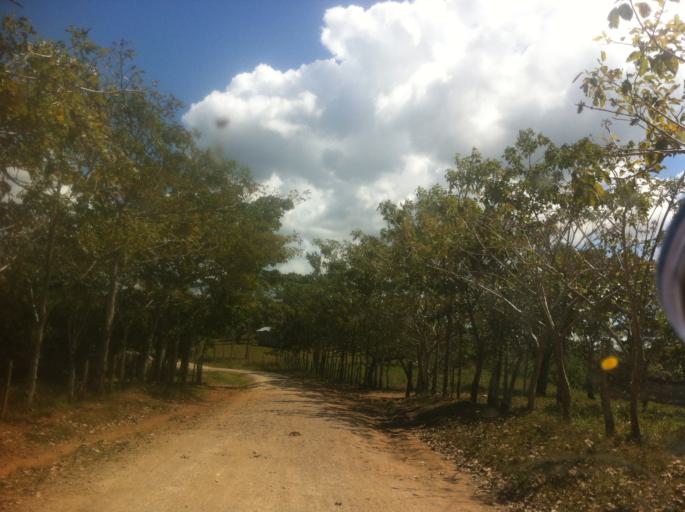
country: NI
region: Rio San Juan
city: San Carlos
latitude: 11.2380
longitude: -84.5271
